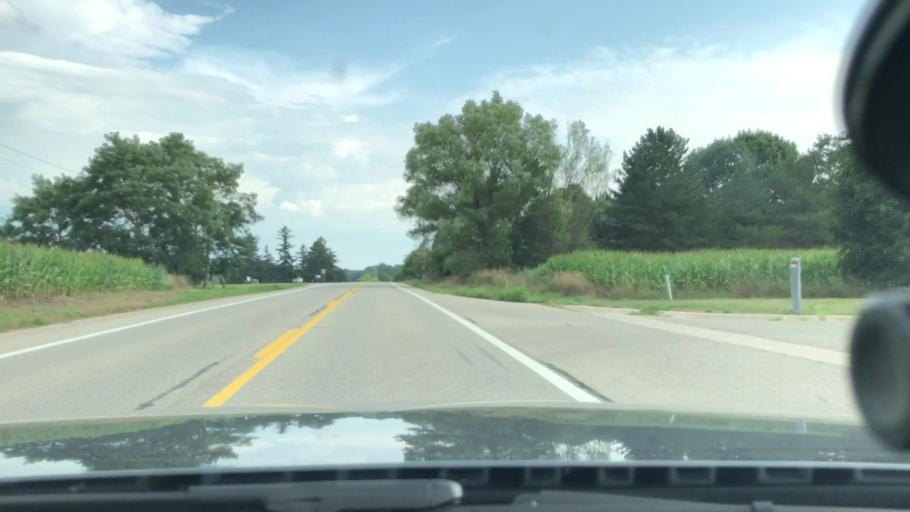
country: US
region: Michigan
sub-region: Washtenaw County
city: Manchester
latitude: 42.1723
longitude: -84.0317
